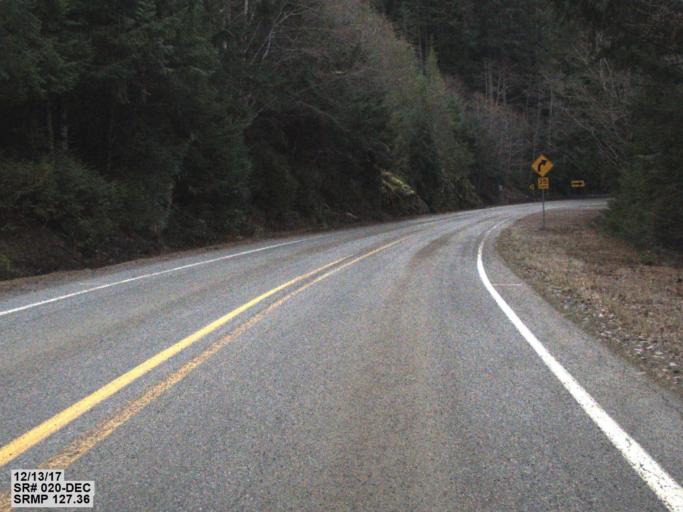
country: US
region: Washington
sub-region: Snohomish County
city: Darrington
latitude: 48.7091
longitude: -121.1363
